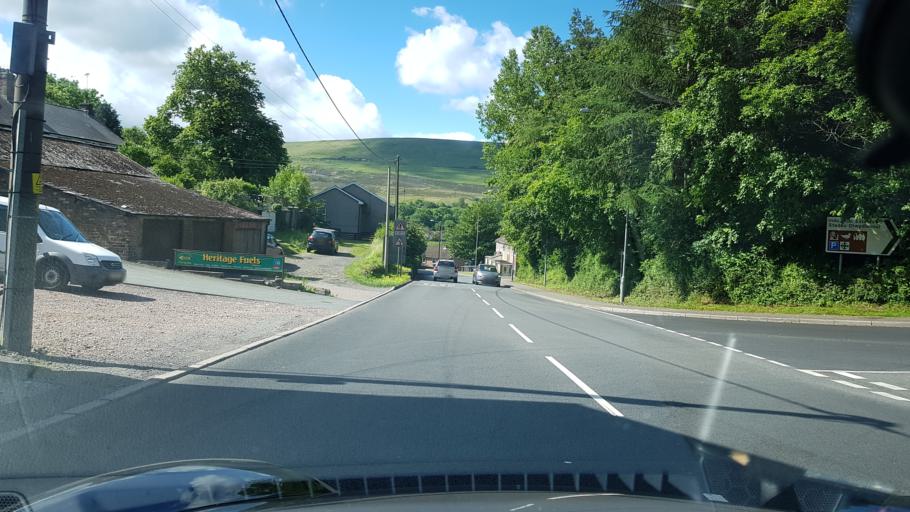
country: GB
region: Wales
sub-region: Torfaen County Borough
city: Blaenavon
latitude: 51.7760
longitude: -3.0894
